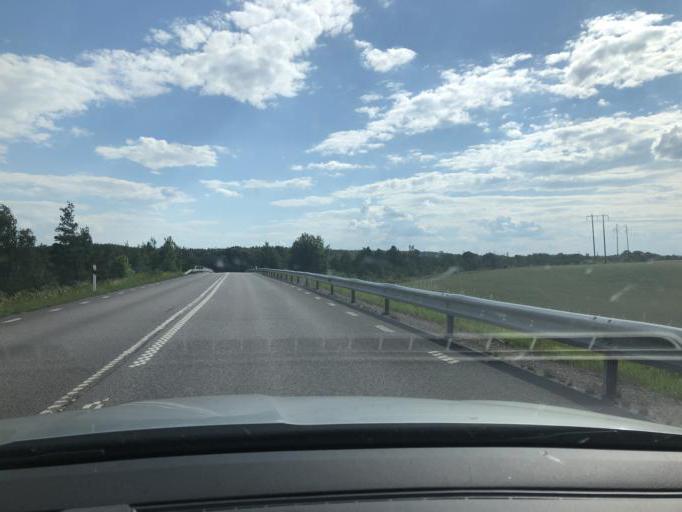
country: SE
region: OEstergoetland
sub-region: Mjolby Kommun
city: Mjolby
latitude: 58.3435
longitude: 15.1721
